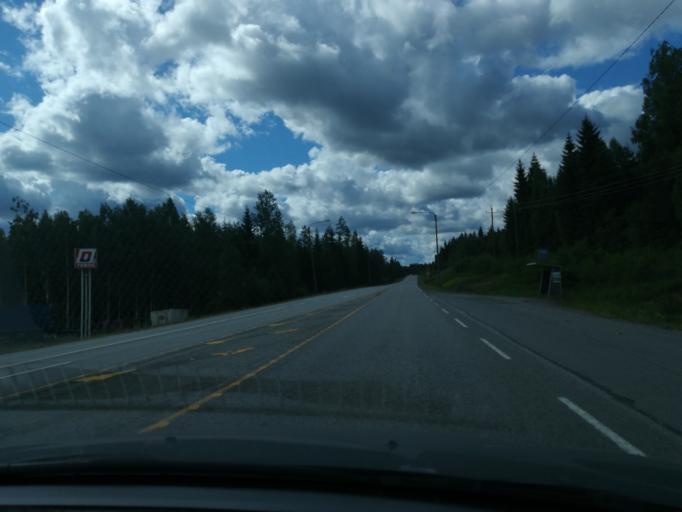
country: FI
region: Southern Savonia
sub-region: Mikkeli
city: Ristiina
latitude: 61.4711
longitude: 27.2551
